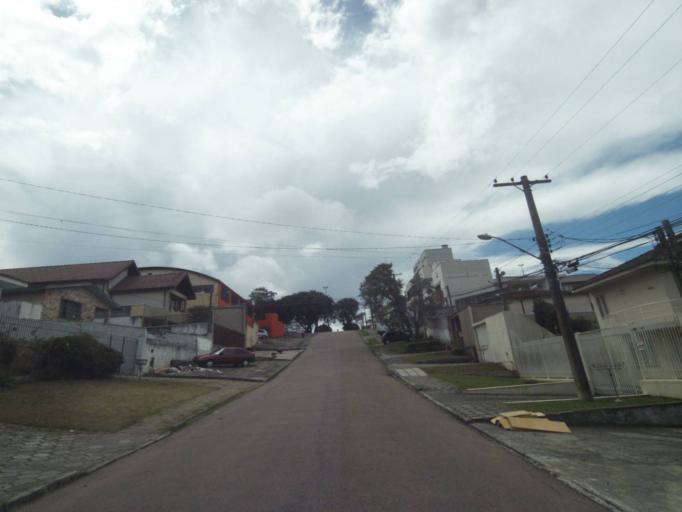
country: BR
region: Parana
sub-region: Curitiba
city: Curitiba
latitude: -25.4775
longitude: -49.2807
